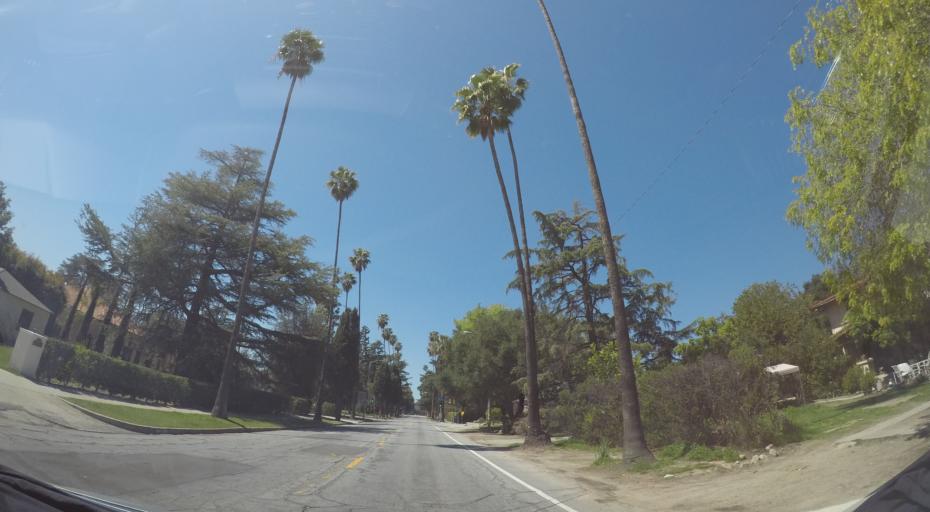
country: US
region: California
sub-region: Los Angeles County
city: Altadena
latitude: 34.1785
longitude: -118.1207
